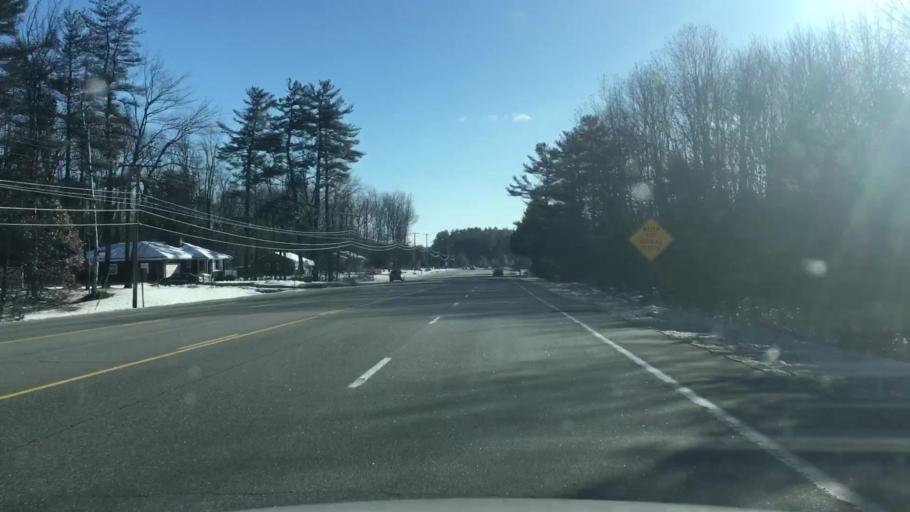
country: US
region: Maine
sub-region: Androscoggin County
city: Auburn
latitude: 44.1584
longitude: -70.2338
